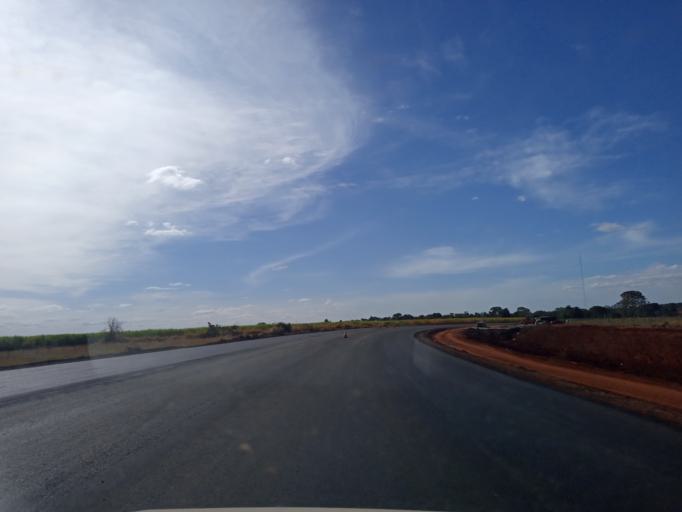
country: BR
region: Minas Gerais
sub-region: Ituiutaba
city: Ituiutaba
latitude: -18.9850
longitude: -49.5112
